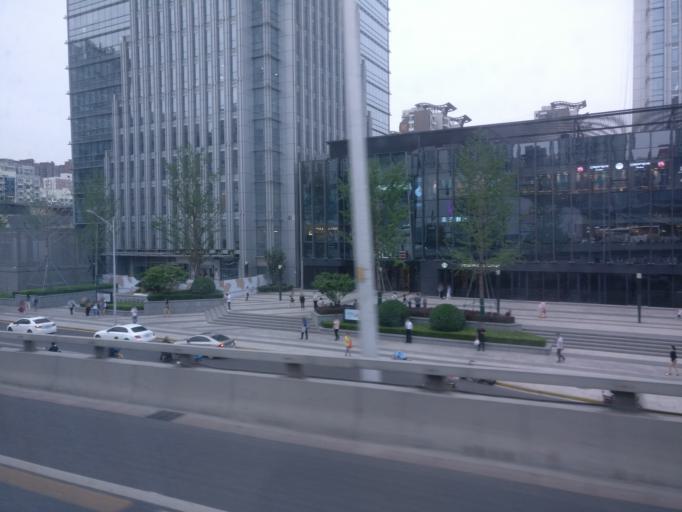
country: CN
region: Beijing
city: Longtan
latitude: 39.8929
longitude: 116.4554
